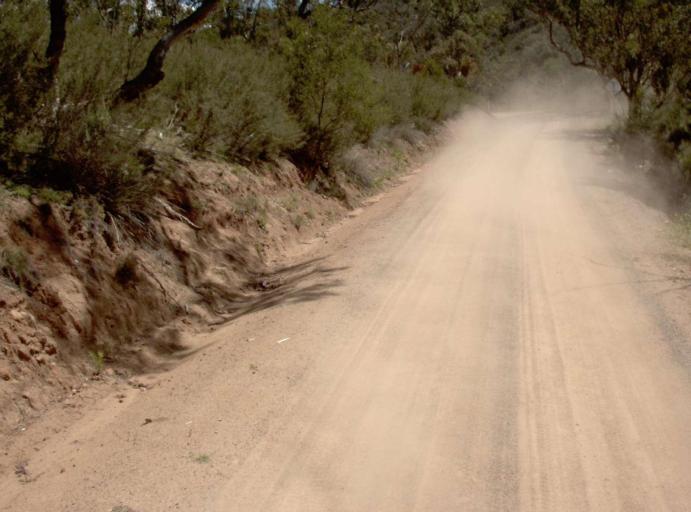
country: AU
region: New South Wales
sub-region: Snowy River
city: Jindabyne
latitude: -37.0372
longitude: 148.5389
